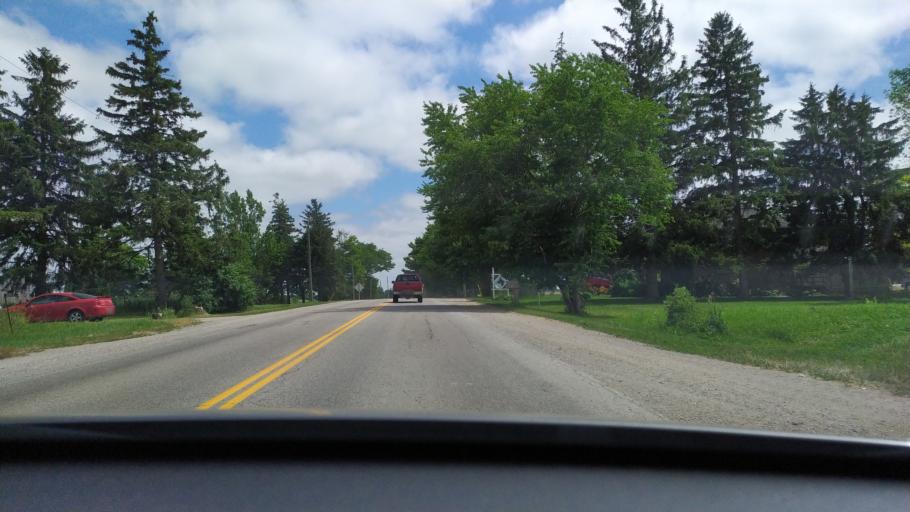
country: CA
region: Ontario
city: Stratford
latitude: 43.3144
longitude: -80.9835
